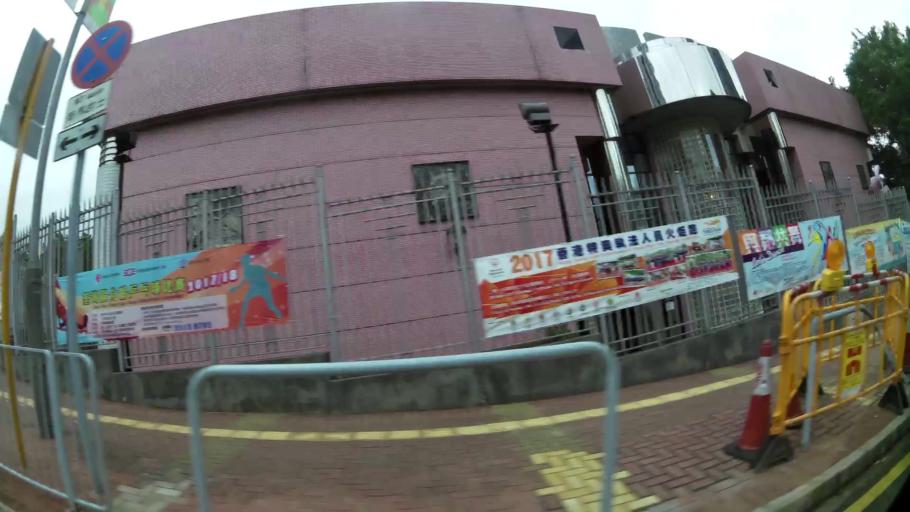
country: HK
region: Tsuen Wan
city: Tsuen Wan
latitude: 22.3721
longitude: 114.1221
